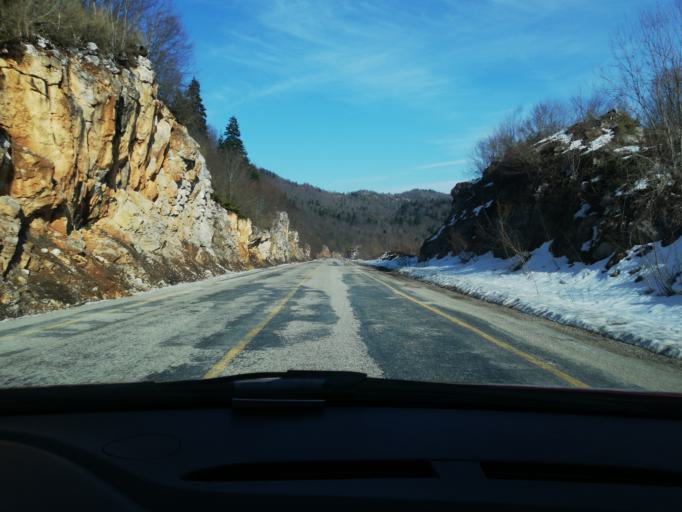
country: TR
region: Kastamonu
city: Cide
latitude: 41.8150
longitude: 33.0953
